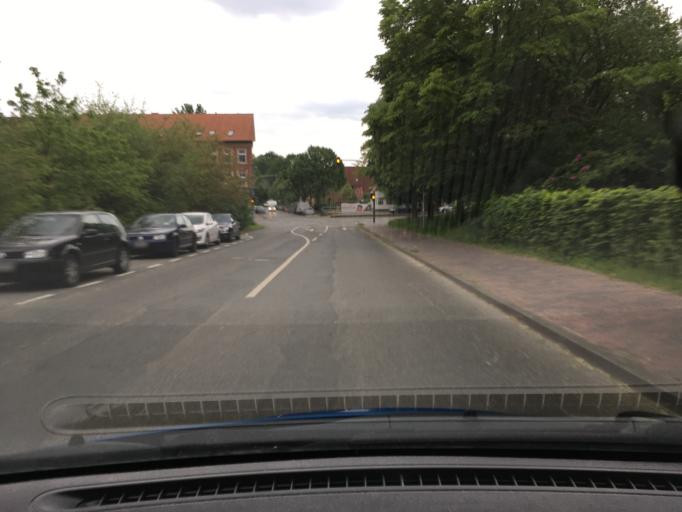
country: DE
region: Lower Saxony
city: Lueneburg
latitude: 53.2500
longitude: 10.3842
